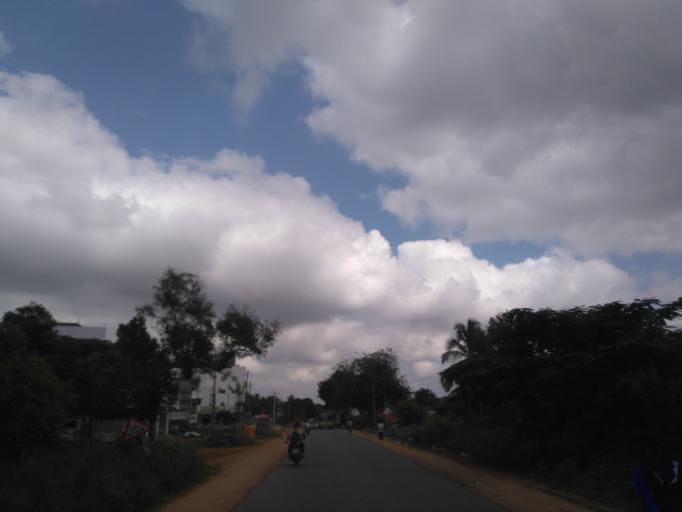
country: IN
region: Karnataka
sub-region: Mysore
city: Mysore
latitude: 12.2784
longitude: 76.7304
